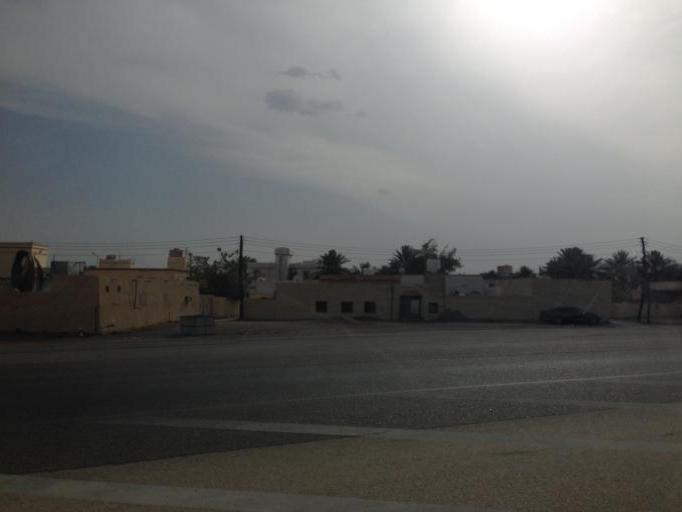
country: OM
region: Ash Sharqiyah
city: Al Qabil
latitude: 22.5715
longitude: 58.6969
